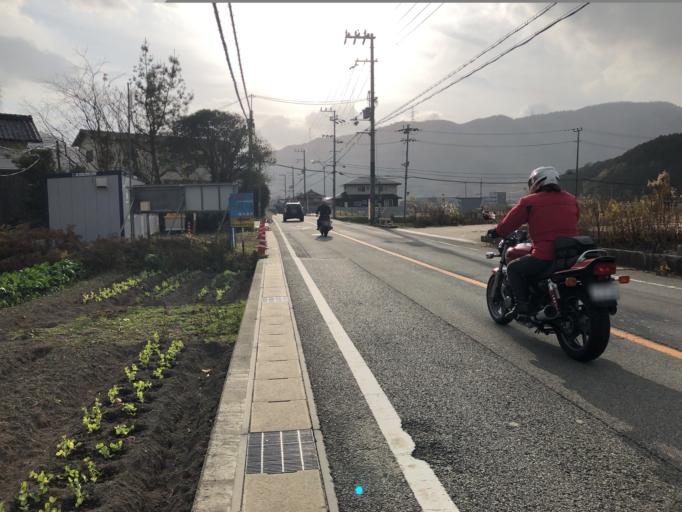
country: JP
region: Kyoto
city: Kameoka
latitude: 35.0092
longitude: 135.4847
